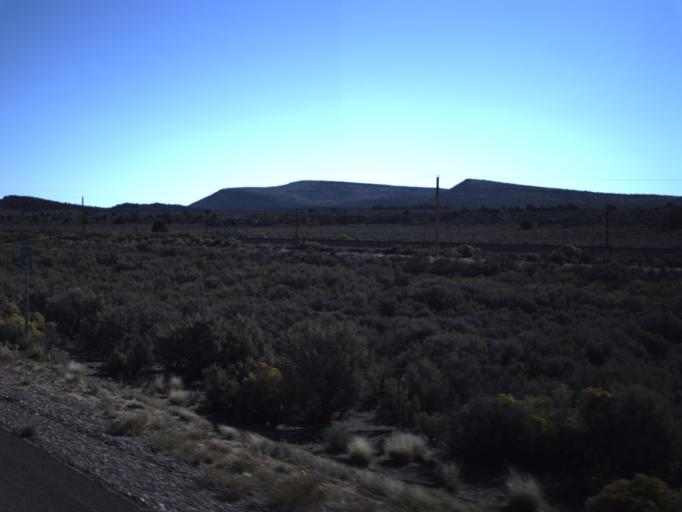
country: US
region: Utah
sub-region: Washington County
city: Enterprise
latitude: 37.7558
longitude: -113.9941
